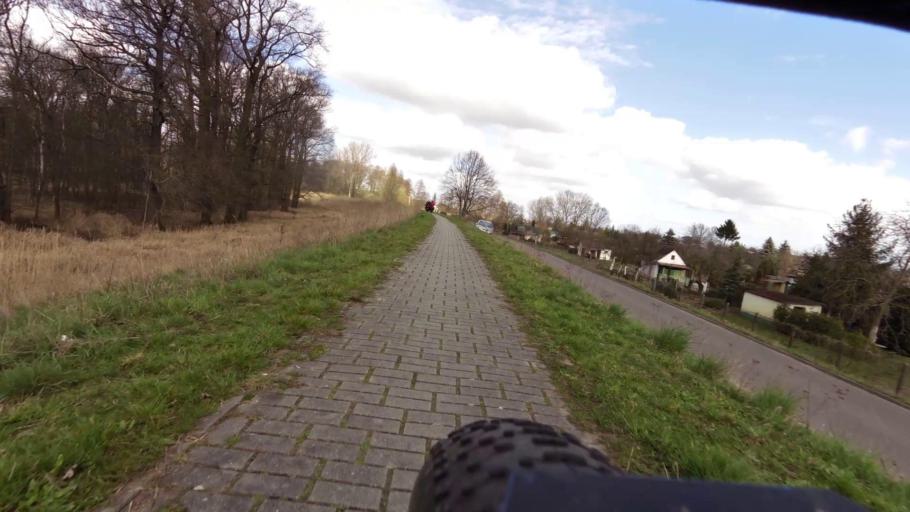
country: PL
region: Lubusz
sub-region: Powiat slubicki
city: Slubice
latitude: 52.3691
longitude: 14.5632
